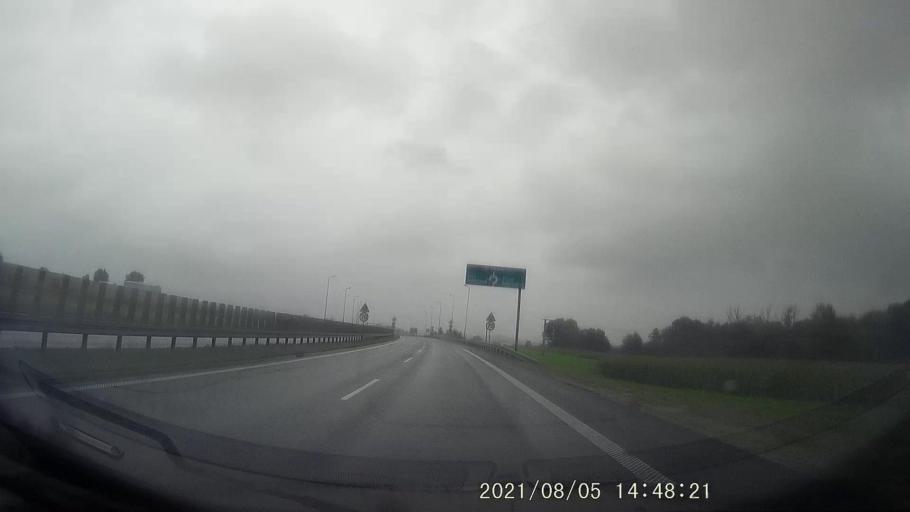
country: PL
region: Opole Voivodeship
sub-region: Powiat nyski
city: Nysa
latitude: 50.4989
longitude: 17.2934
